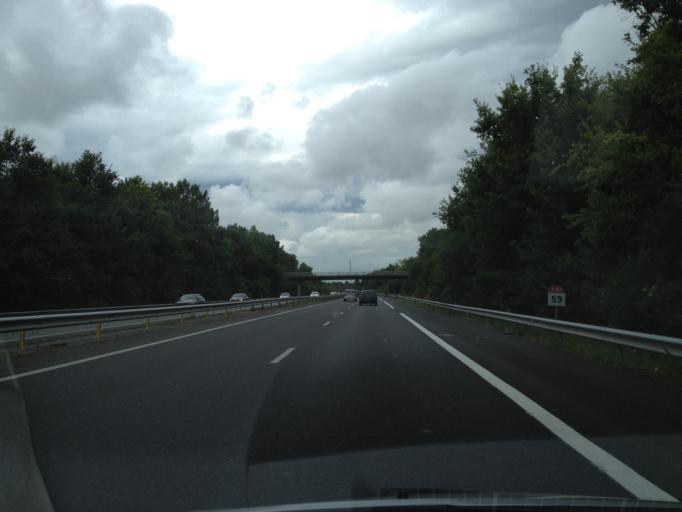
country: FR
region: Aquitaine
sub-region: Departement du Lot-et-Garonne
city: Meilhan-sur-Garonne
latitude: 44.4875
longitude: 0.0060
